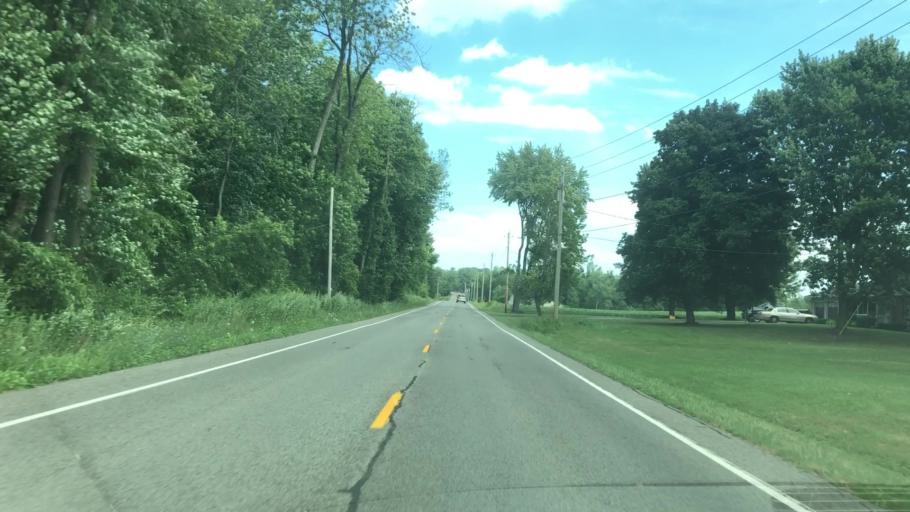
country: US
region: New York
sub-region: Wayne County
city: Macedon
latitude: 43.1163
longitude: -77.3525
